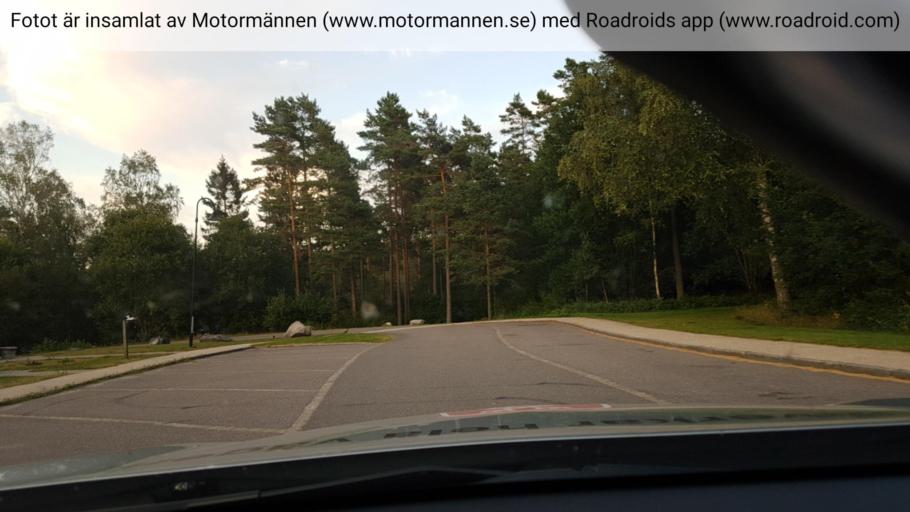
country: SE
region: Vaestra Goetaland
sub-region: Harryda Kommun
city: Ravlanda
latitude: 57.6696
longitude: 12.4931
